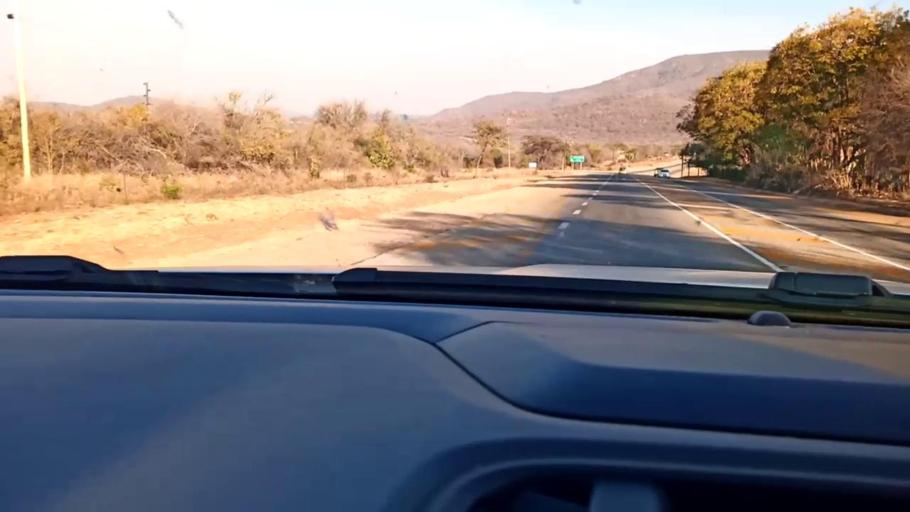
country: ZA
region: Limpopo
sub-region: Mopani District Municipality
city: Duiwelskloof
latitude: -23.6237
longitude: 30.1286
